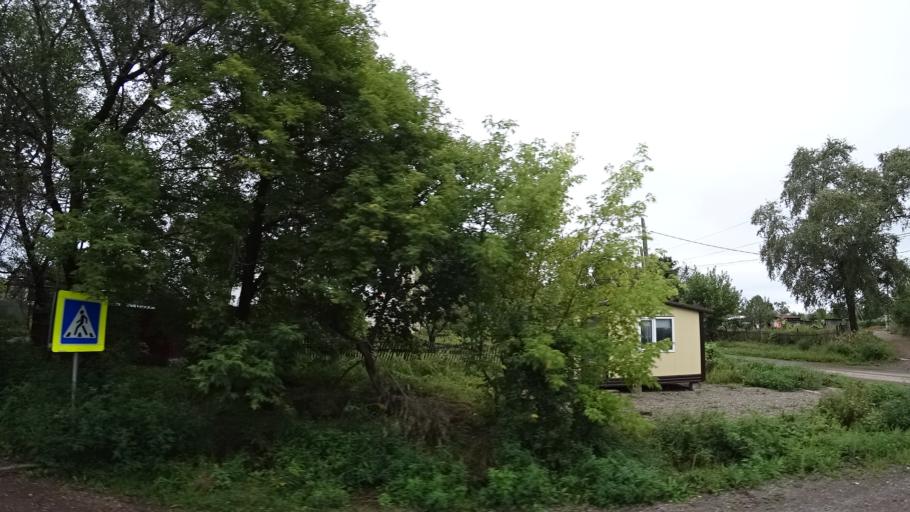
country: RU
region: Primorskiy
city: Chernigovka
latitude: 44.3390
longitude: 132.5444
